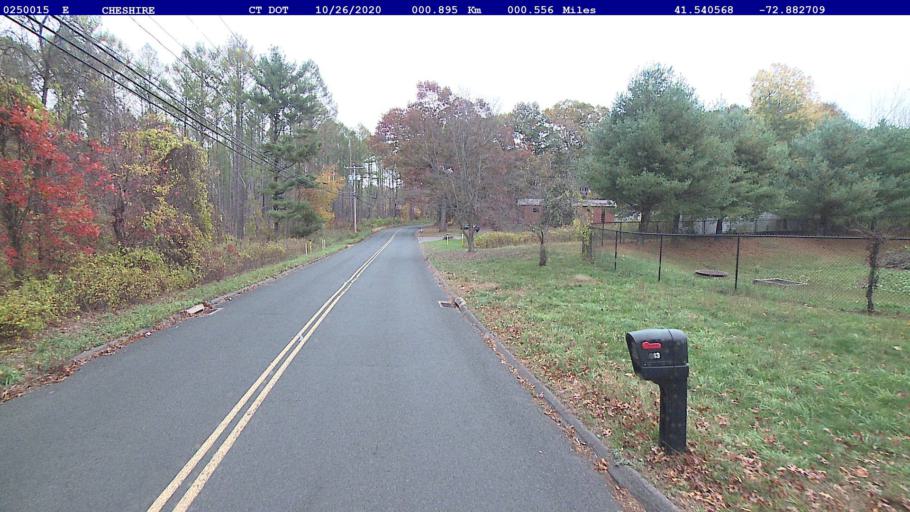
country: US
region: Connecticut
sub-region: New Haven County
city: Cheshire Village
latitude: 41.5405
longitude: -72.8827
